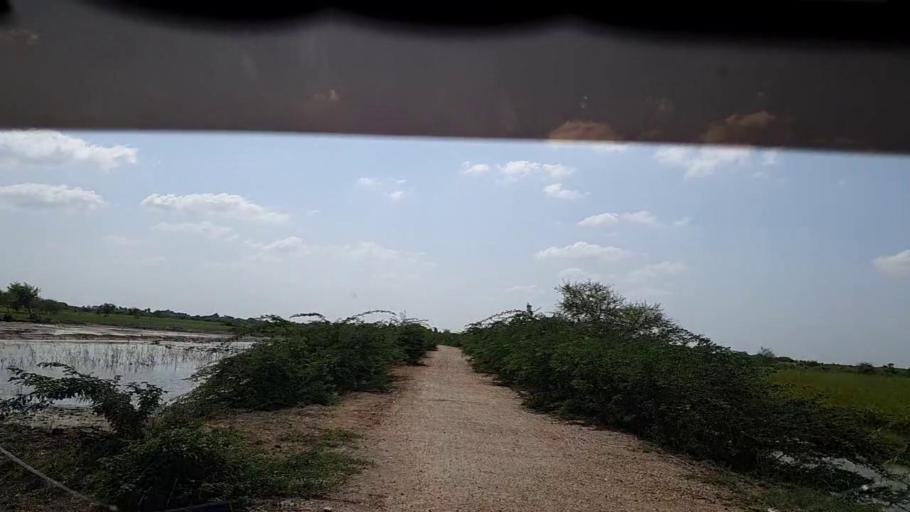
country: PK
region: Sindh
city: Kadhan
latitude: 24.5930
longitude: 69.0218
